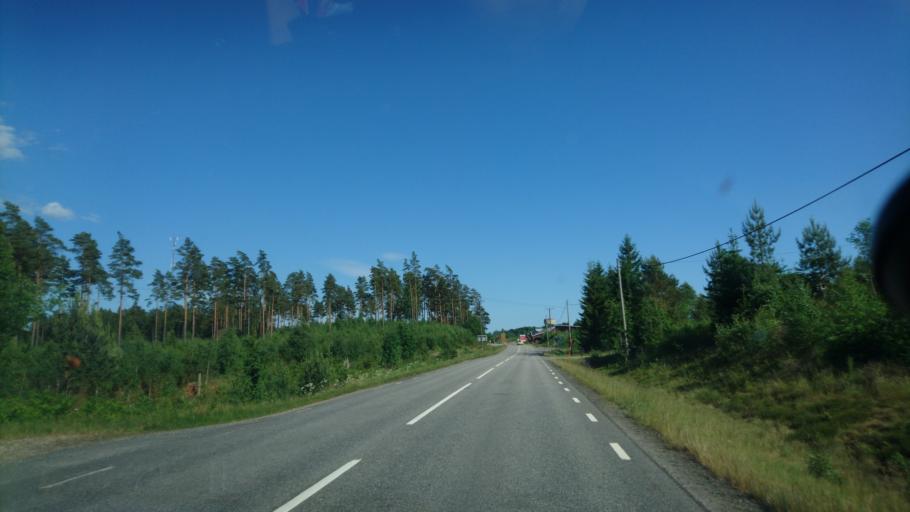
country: SE
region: Skane
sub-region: Osby Kommun
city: Lonsboda
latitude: 56.4115
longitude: 14.3047
